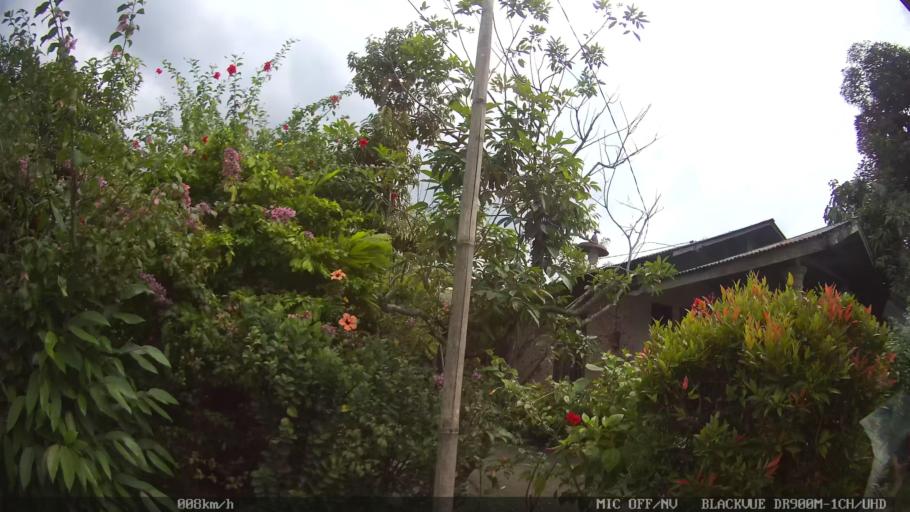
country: ID
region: North Sumatra
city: Sunggal
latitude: 3.6242
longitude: 98.5944
